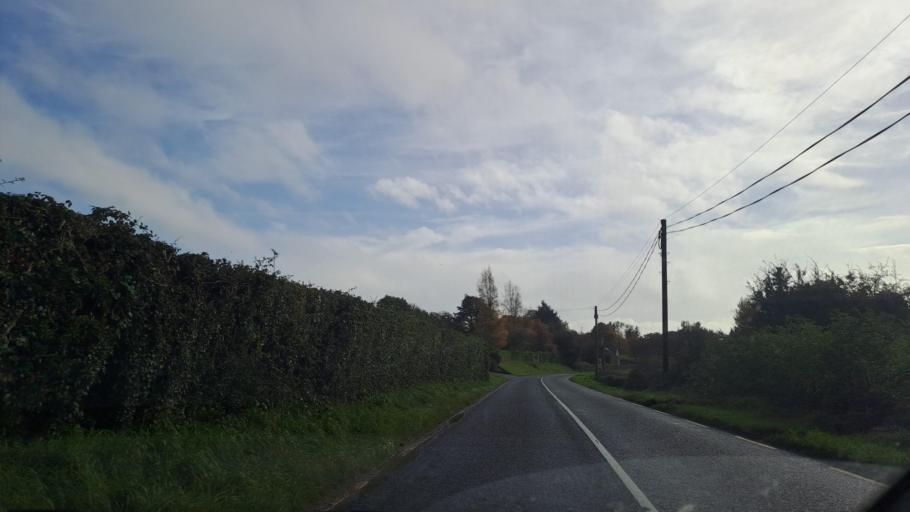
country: IE
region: Ulster
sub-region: County Monaghan
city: Carrickmacross
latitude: 53.9238
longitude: -6.7137
